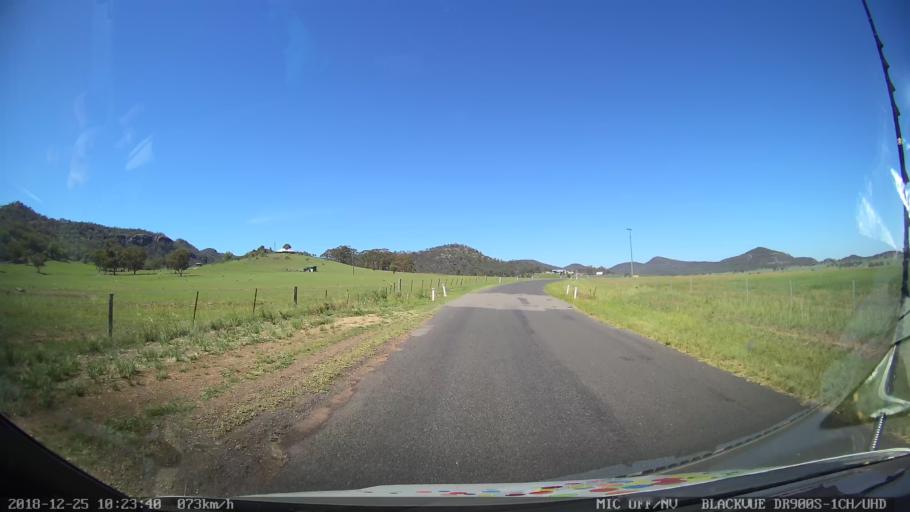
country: AU
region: New South Wales
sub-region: Muswellbrook
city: Denman
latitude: -32.3882
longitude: 150.5219
